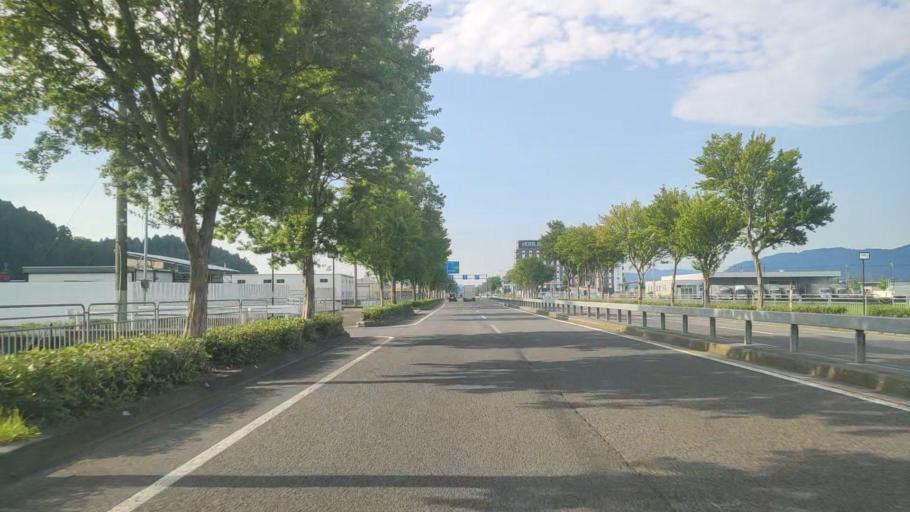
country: JP
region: Fukui
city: Takefu
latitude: 35.8999
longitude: 136.1923
